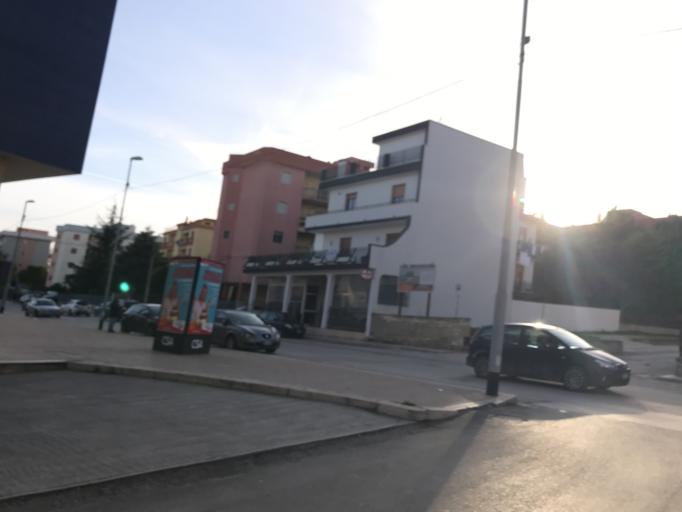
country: IT
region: Apulia
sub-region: Provincia di Bari
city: Corato
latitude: 41.1461
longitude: 16.4096
